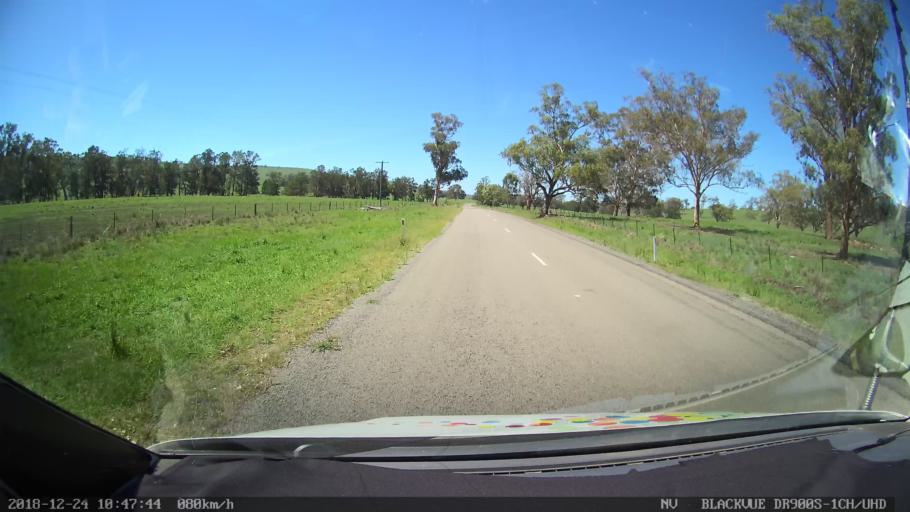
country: AU
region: New South Wales
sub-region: Upper Hunter Shire
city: Merriwa
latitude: -31.9279
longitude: 150.4298
